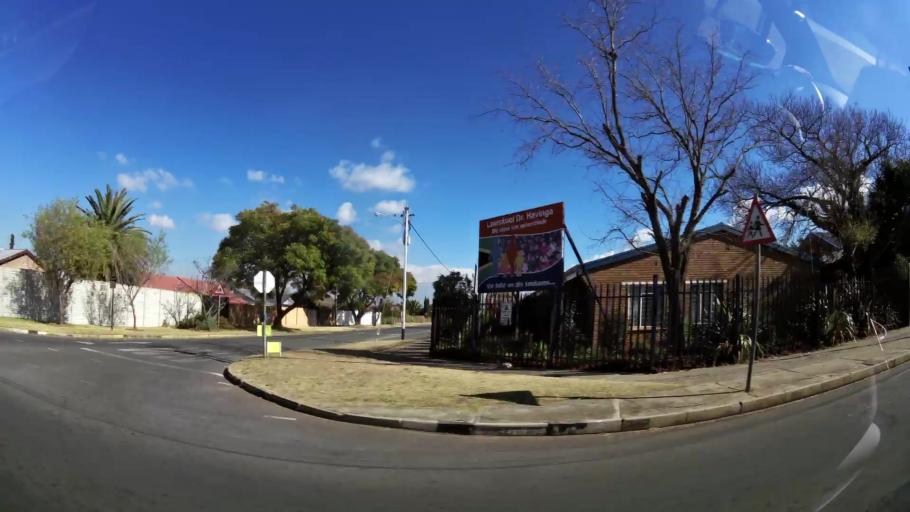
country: ZA
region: Gauteng
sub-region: City of Johannesburg Metropolitan Municipality
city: Roodepoort
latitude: -26.1397
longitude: 27.8361
